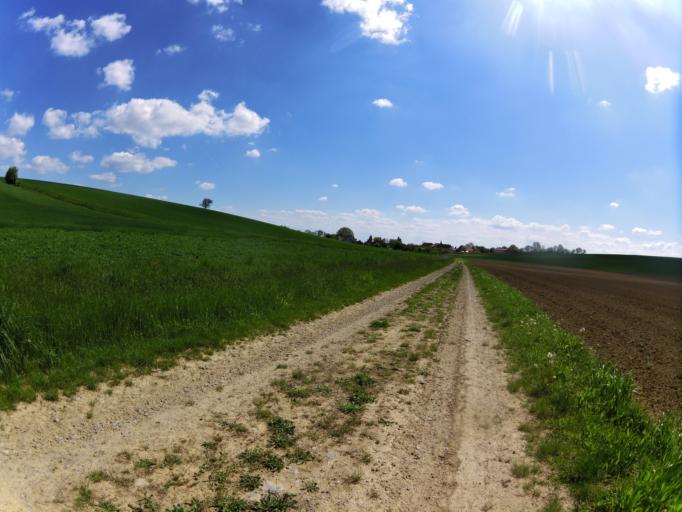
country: DE
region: Bavaria
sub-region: Regierungsbezirk Unterfranken
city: Unterpleichfeld
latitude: 49.8866
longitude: 10.0040
